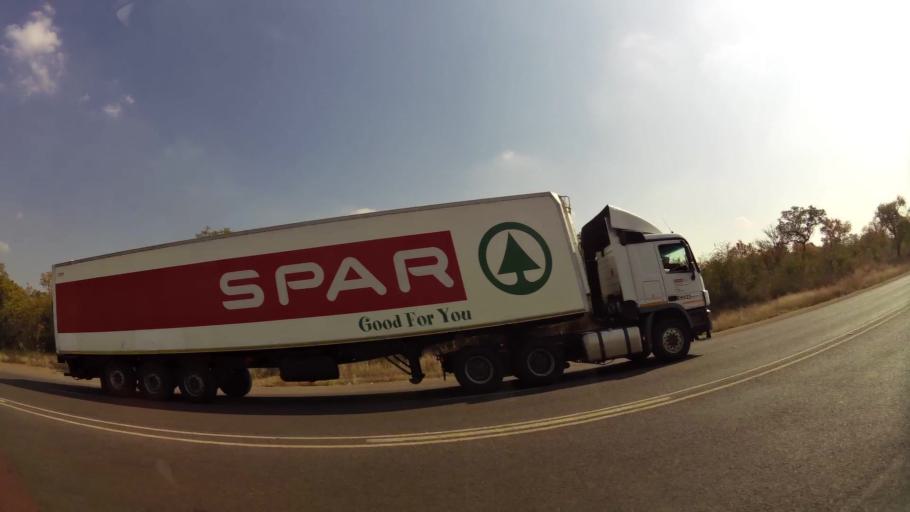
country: ZA
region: North-West
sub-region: Bojanala Platinum District Municipality
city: Mogwase
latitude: -25.4494
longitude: 27.0879
